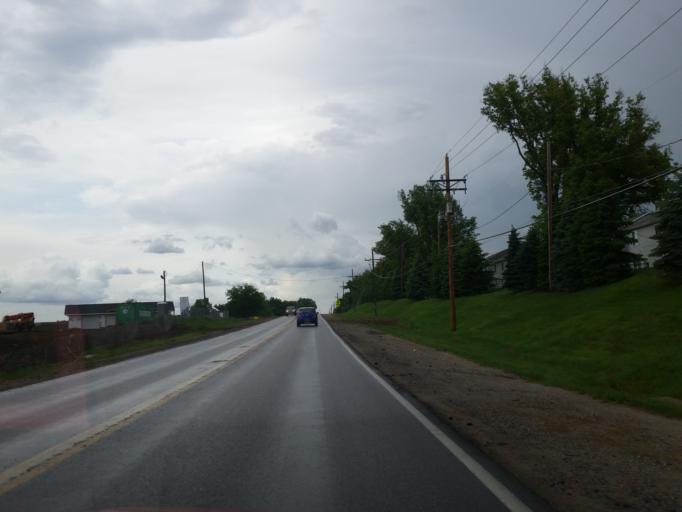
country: US
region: Nebraska
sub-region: Sarpy County
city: Offutt Air Force Base
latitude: 41.1228
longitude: -95.9666
